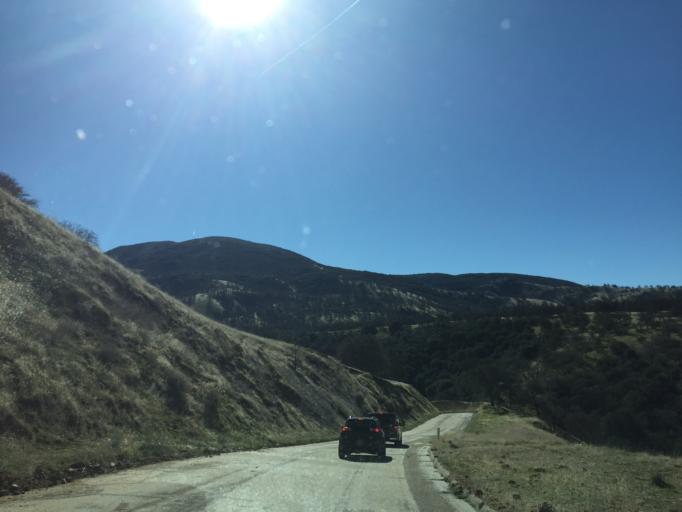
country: US
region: California
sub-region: Kern County
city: Lebec
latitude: 34.8874
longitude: -118.7820
